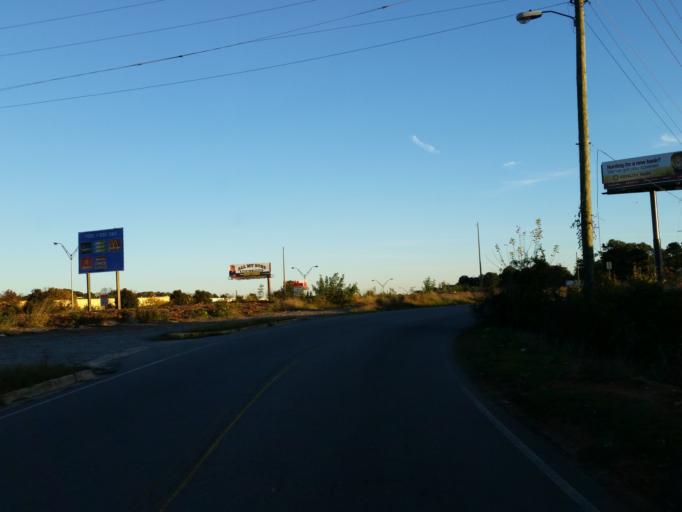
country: US
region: Georgia
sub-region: Cobb County
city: Marietta
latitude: 33.9498
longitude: -84.5170
